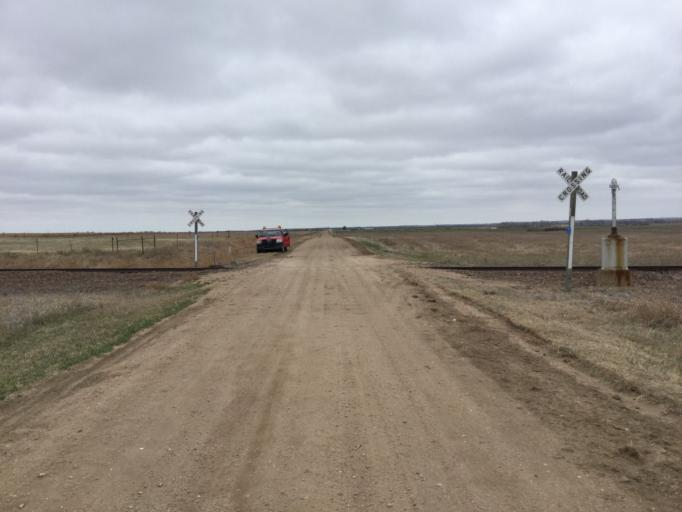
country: US
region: Kansas
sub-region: Barton County
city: Ellinwood
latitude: 38.5104
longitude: -98.6091
